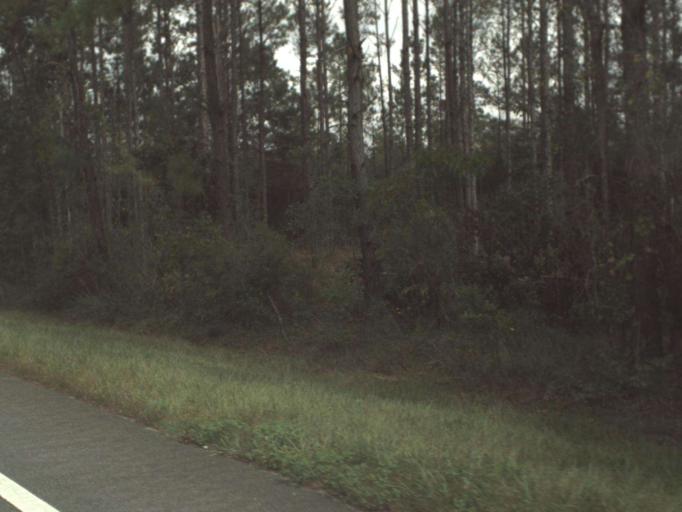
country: US
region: Florida
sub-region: Calhoun County
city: Blountstown
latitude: 30.3471
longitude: -85.2152
